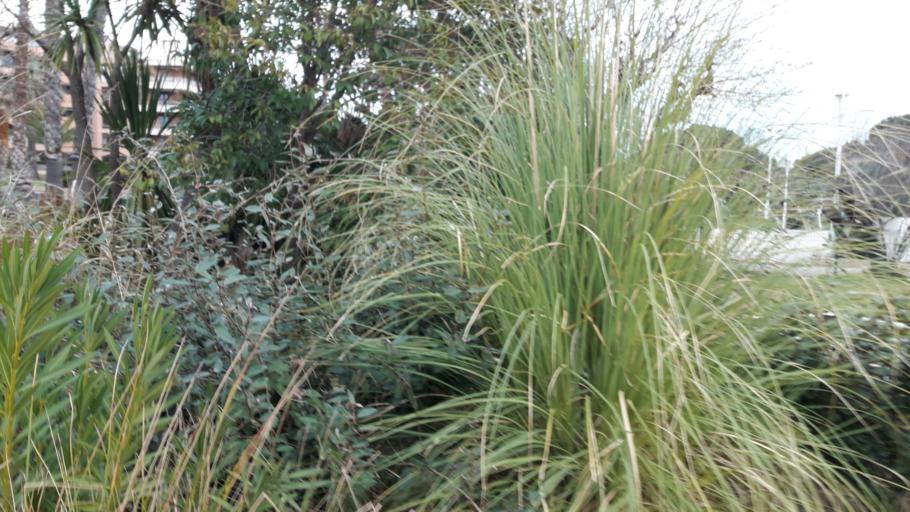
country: FR
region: Provence-Alpes-Cote d'Azur
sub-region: Departement du Var
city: Saint-Raphael
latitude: 43.4185
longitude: 6.7731
